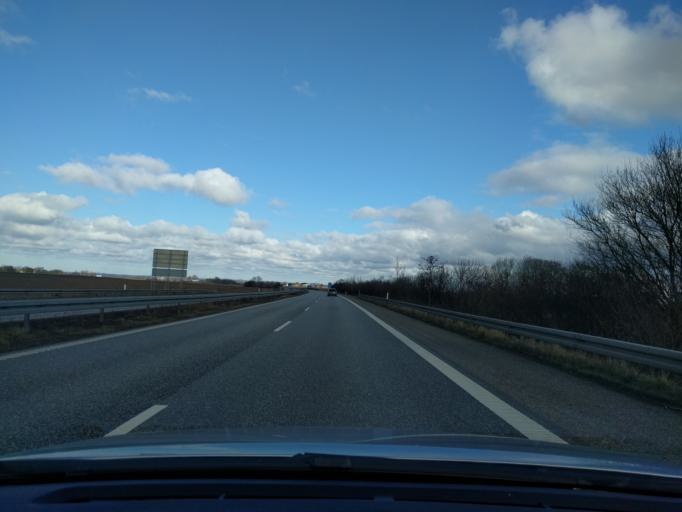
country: DK
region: Zealand
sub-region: Guldborgsund Kommune
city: Norre Alslev
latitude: 54.8847
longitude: 11.9121
